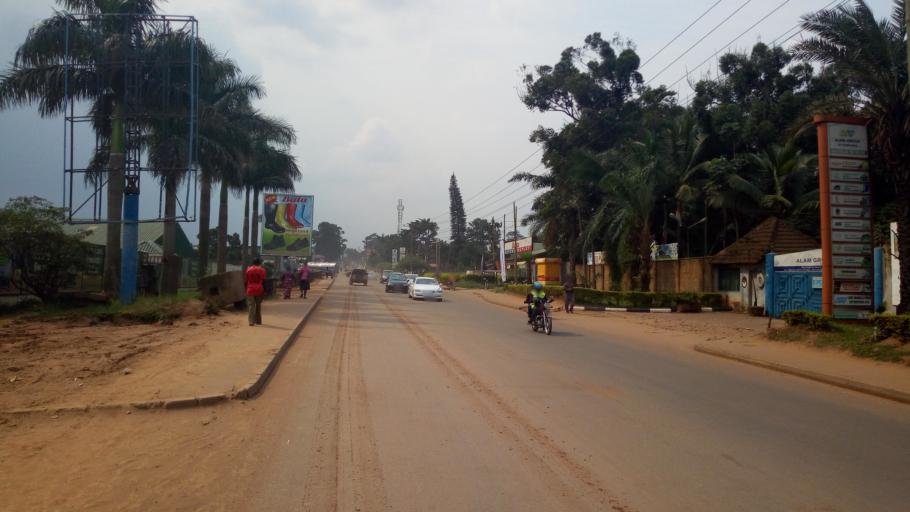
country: UG
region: Central Region
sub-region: Kampala District
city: Kampala
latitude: 0.3160
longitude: 32.6114
